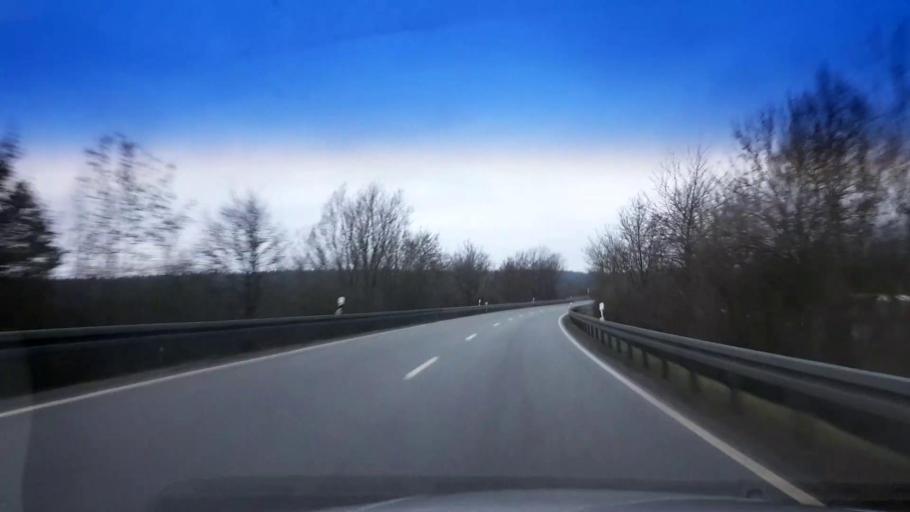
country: DE
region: Bavaria
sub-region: Upper Palatinate
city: Tirschenreuth
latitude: 49.8646
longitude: 12.2585
